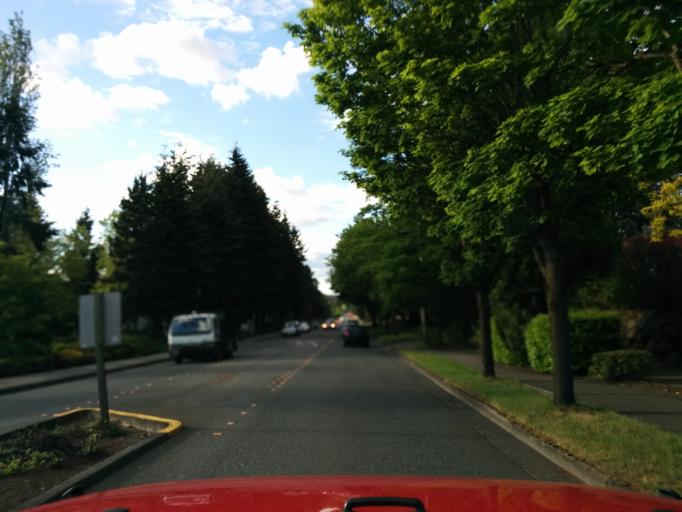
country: US
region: Washington
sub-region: King County
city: Bellevue
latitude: 47.6214
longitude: -122.1537
